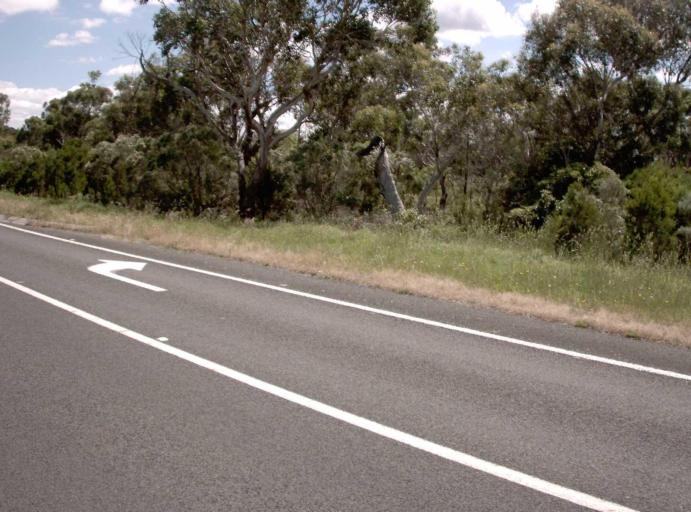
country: AU
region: Victoria
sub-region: Cardinia
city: Koo-Wee-Rup
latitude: -38.3604
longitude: 145.5613
